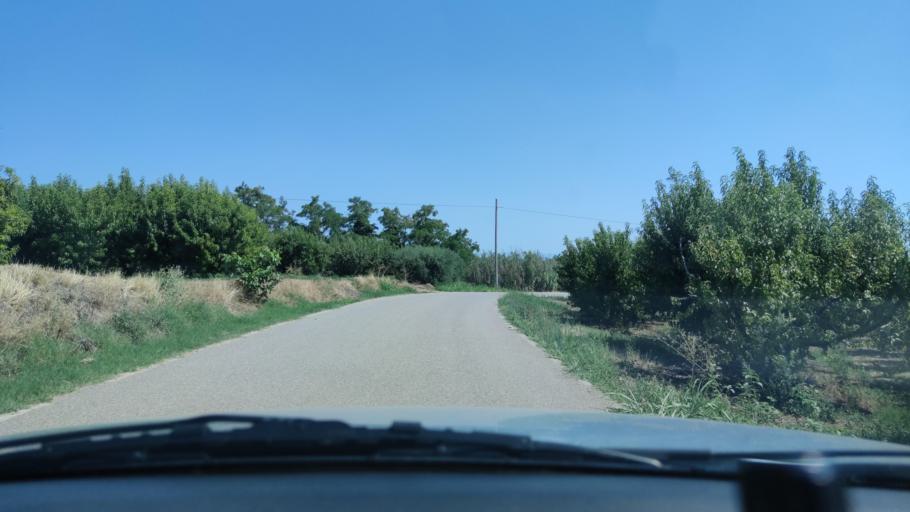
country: ES
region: Catalonia
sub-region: Provincia de Lleida
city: Torrefarrera
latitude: 41.6878
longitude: 0.6246
